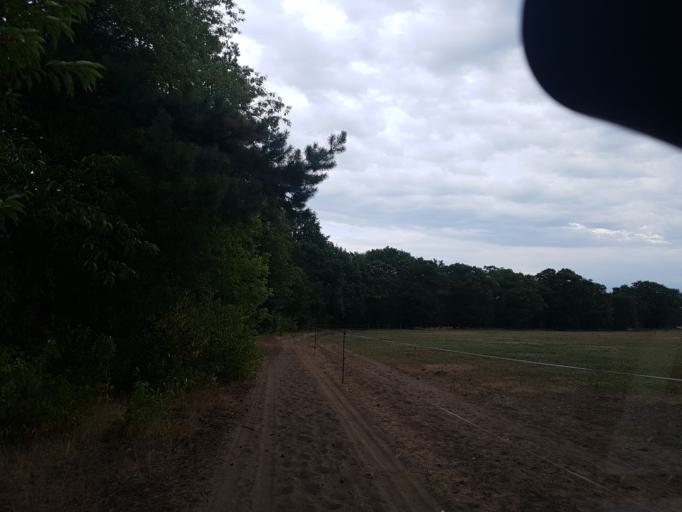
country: DE
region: Brandenburg
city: Schilda
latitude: 51.5718
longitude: 13.3442
